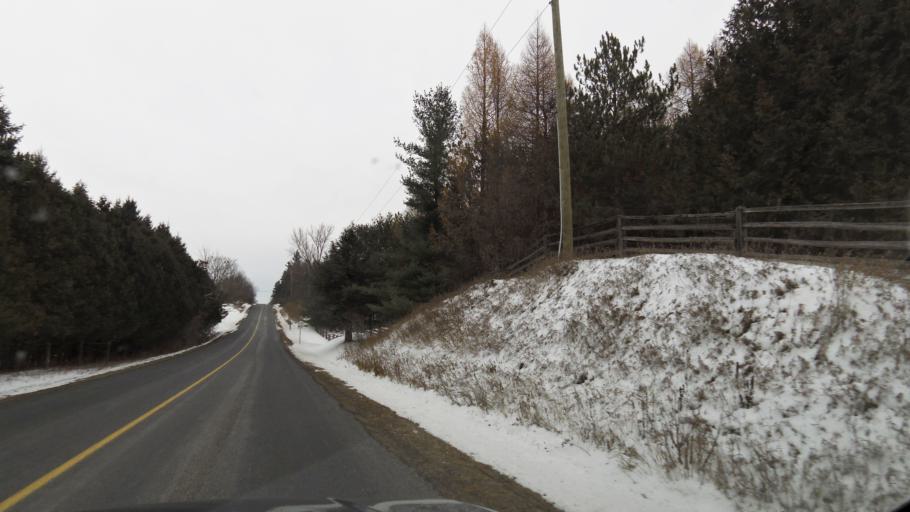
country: CA
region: Ontario
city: Bradford West Gwillimbury
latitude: 43.9503
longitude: -79.6385
